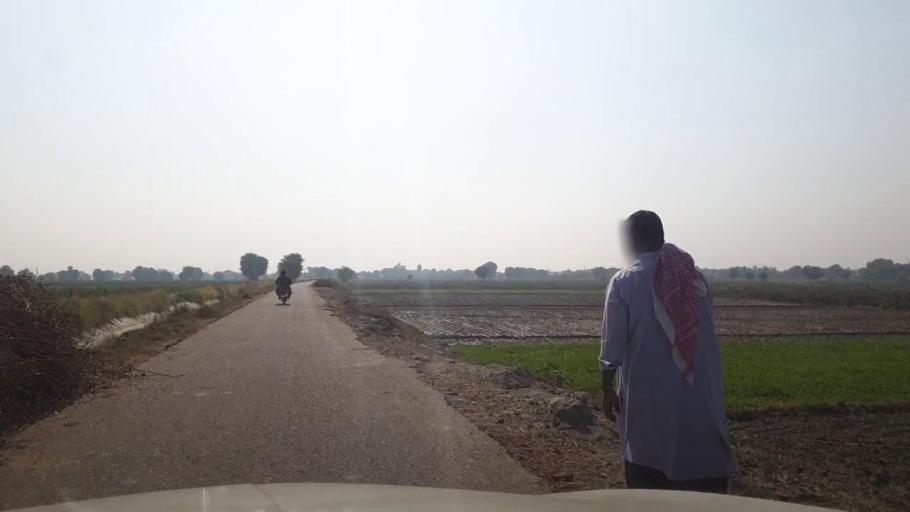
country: PK
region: Sindh
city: Bhan
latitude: 26.5242
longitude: 67.7794
